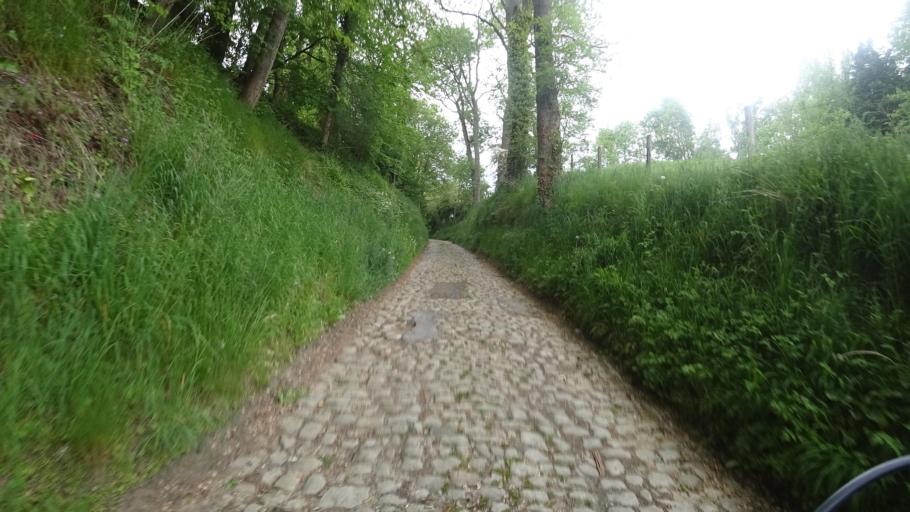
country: BE
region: Wallonia
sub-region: Province du Brabant Wallon
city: Walhain-Saint-Paul
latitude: 50.6671
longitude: 4.6699
